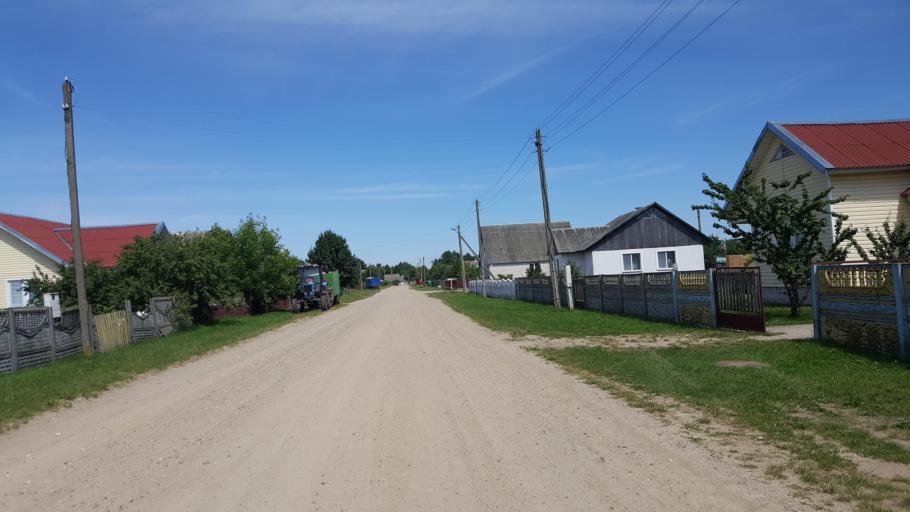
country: BY
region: Brest
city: Pruzhany
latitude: 52.5533
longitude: 24.2022
